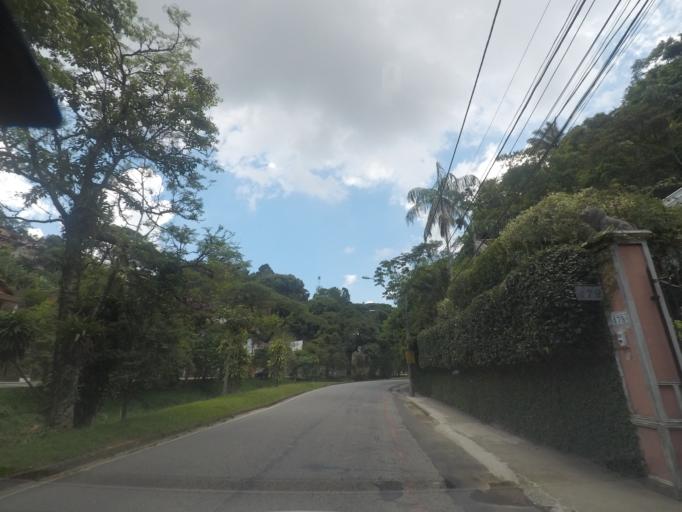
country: BR
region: Rio de Janeiro
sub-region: Petropolis
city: Petropolis
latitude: -22.4995
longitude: -43.1808
